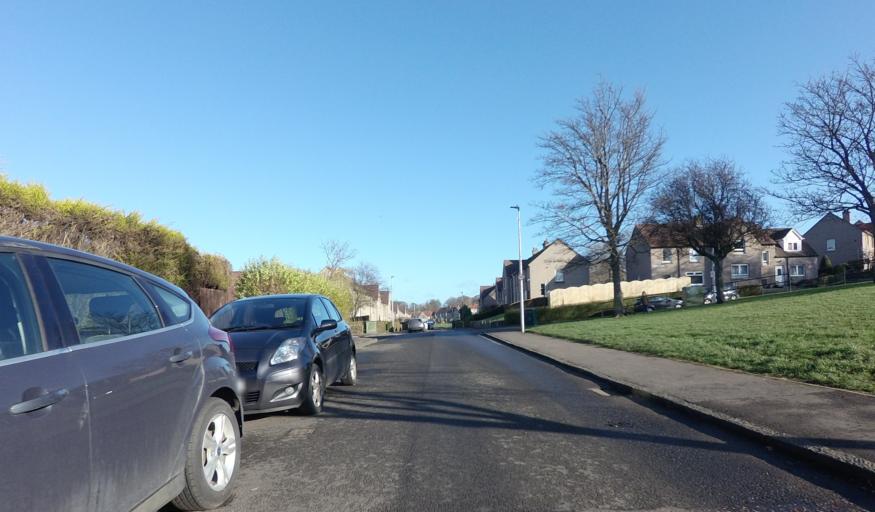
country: GB
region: Scotland
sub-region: Edinburgh
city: Colinton
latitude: 55.9588
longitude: -3.2863
